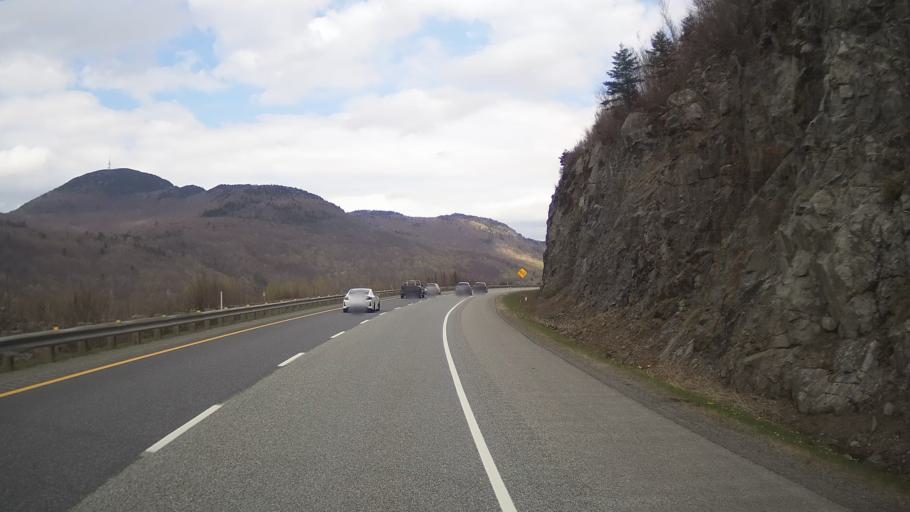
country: CA
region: Quebec
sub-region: Estrie
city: Magog
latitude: 45.2888
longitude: -72.2683
